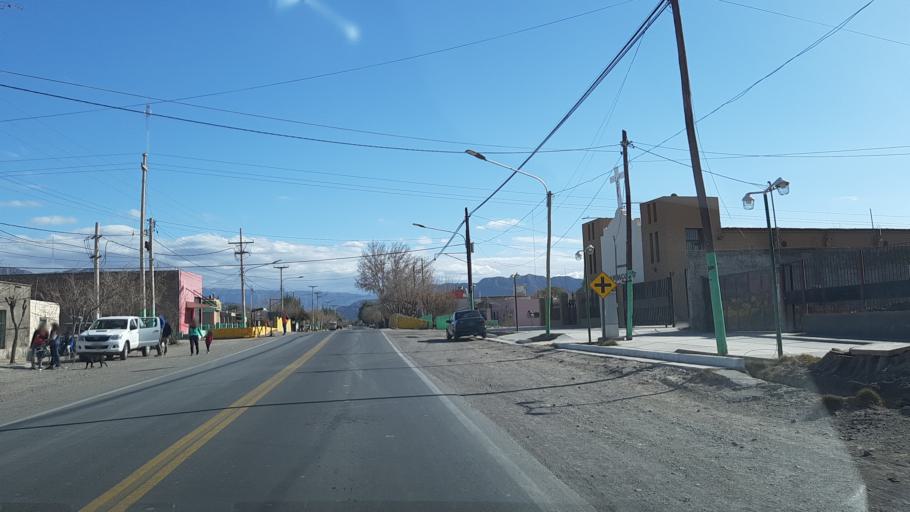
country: AR
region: San Juan
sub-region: Departamento de Rivadavia
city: Rivadavia
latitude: -31.5399
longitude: -68.6181
